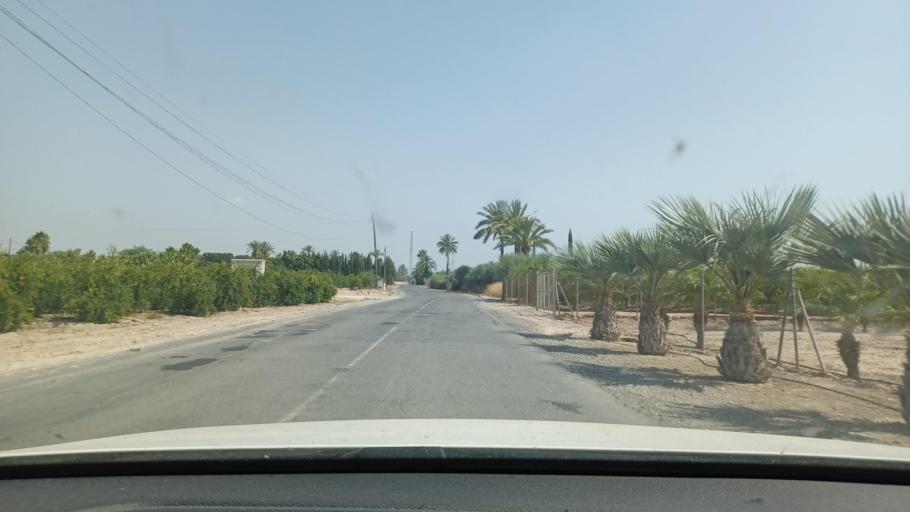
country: ES
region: Valencia
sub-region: Provincia de Alicante
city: Elche
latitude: 38.2268
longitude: -0.6945
